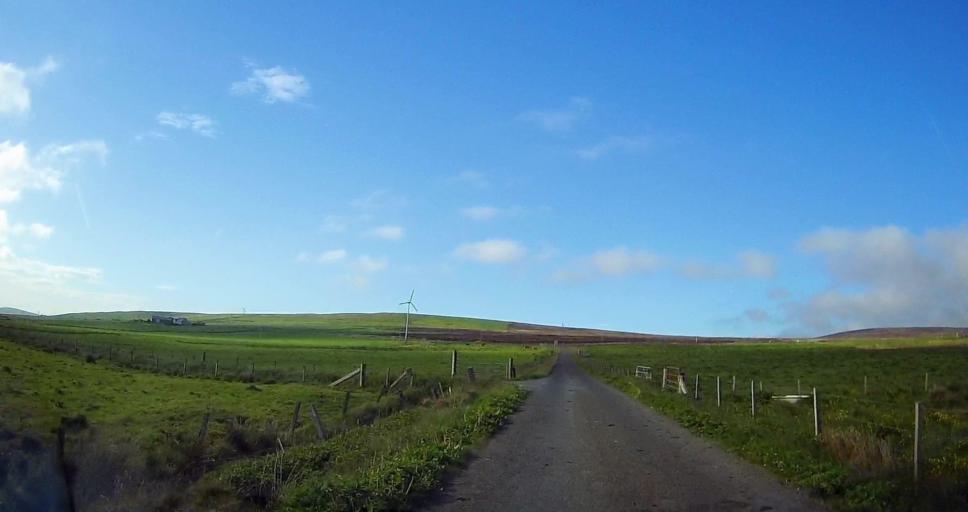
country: GB
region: Scotland
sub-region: Orkney Islands
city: Stromness
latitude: 59.0901
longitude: -3.1831
